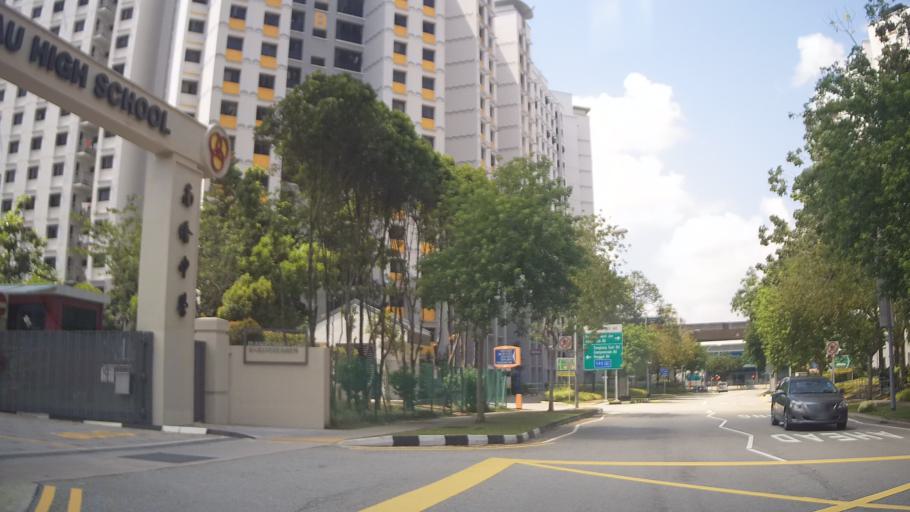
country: MY
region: Johor
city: Kampung Pasir Gudang Baru
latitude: 1.3893
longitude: 103.8891
